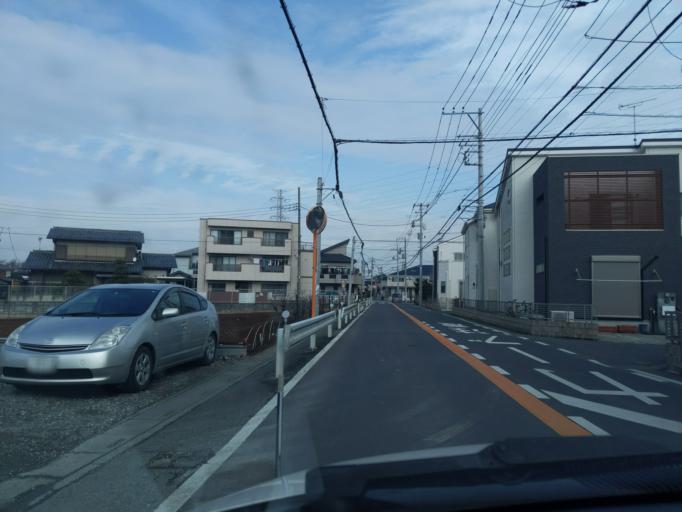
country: JP
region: Saitama
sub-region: Kawaguchi-shi
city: Hatogaya-honcho
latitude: 35.8571
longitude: 139.7276
